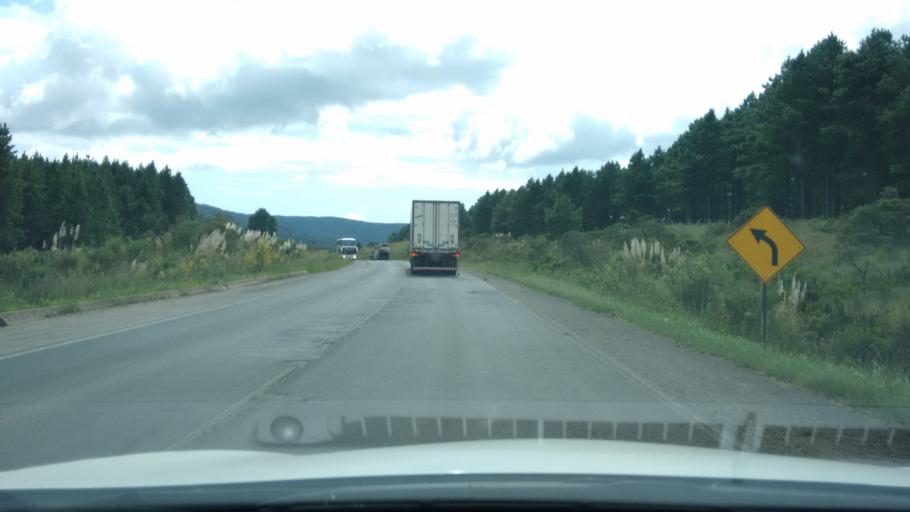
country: BR
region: Santa Catarina
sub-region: Otacilio Costa
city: Otacilio Costa
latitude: -27.3006
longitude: -50.2150
